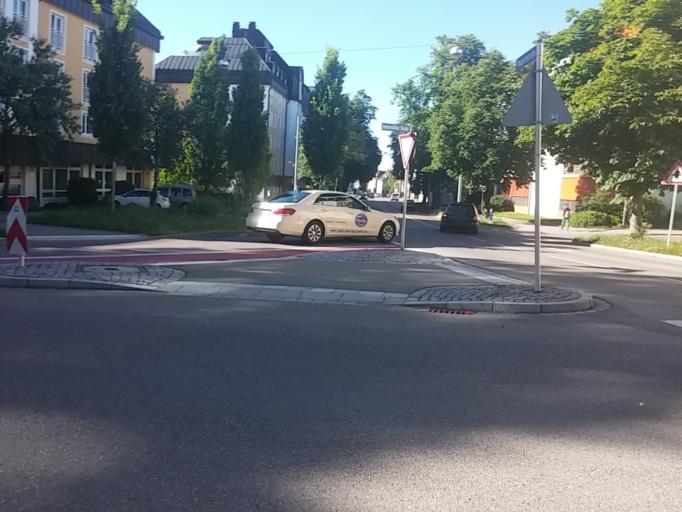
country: DE
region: Bavaria
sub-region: Swabia
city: Kempten (Allgaeu)
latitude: 47.7224
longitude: 10.3114
